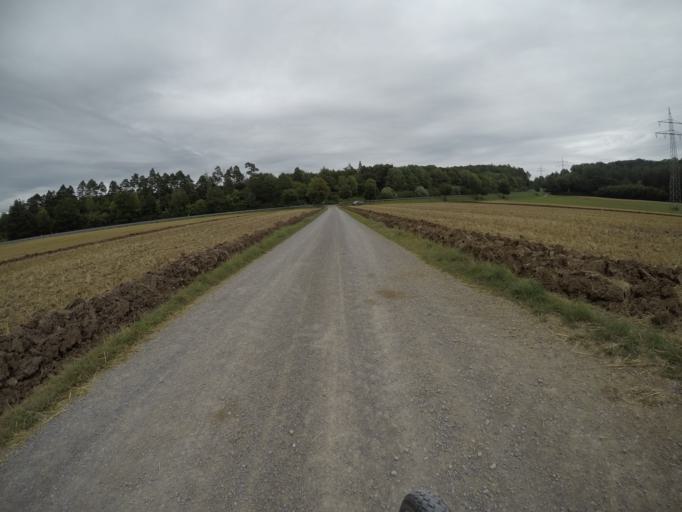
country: DE
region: Baden-Wuerttemberg
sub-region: Regierungsbezirk Stuttgart
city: Ehningen
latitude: 48.6367
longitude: 8.9465
